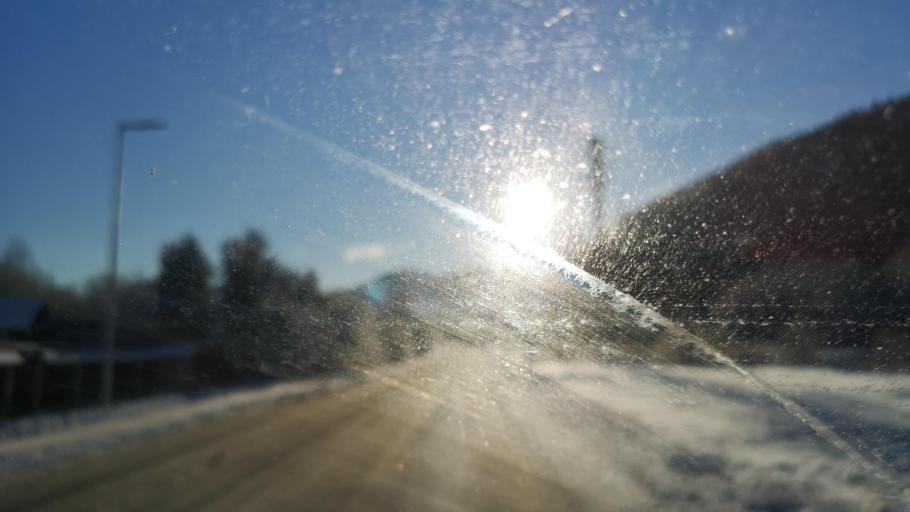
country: SK
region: Banskobystricky
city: Tisovec
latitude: 48.8597
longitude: 19.9793
